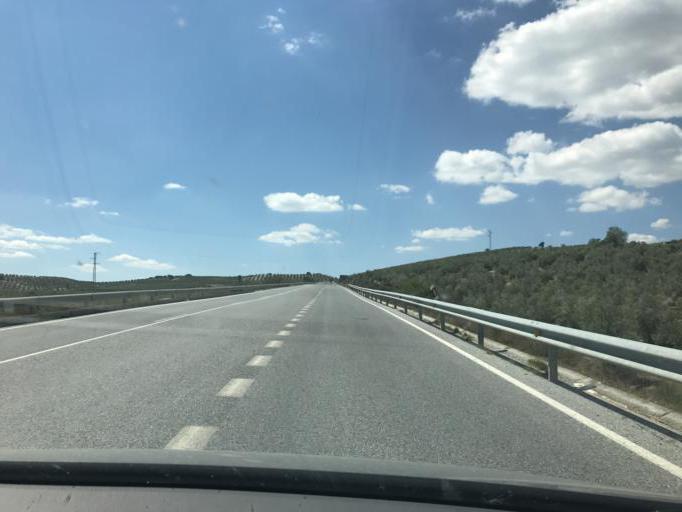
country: ES
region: Andalusia
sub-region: Provincia de Granada
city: Benalua de las Villas
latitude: 37.4279
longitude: -3.7390
